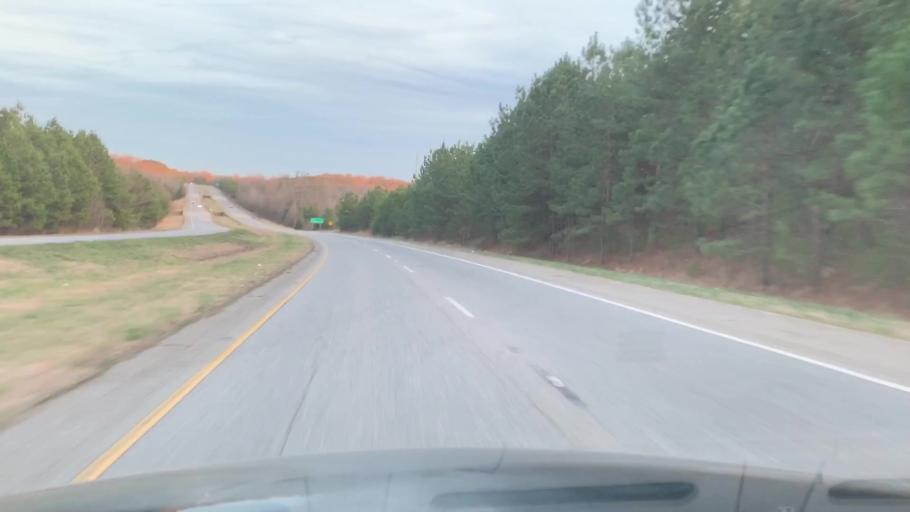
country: US
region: South Carolina
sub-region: Greenville County
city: Golden Grove
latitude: 34.7318
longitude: -82.4238
